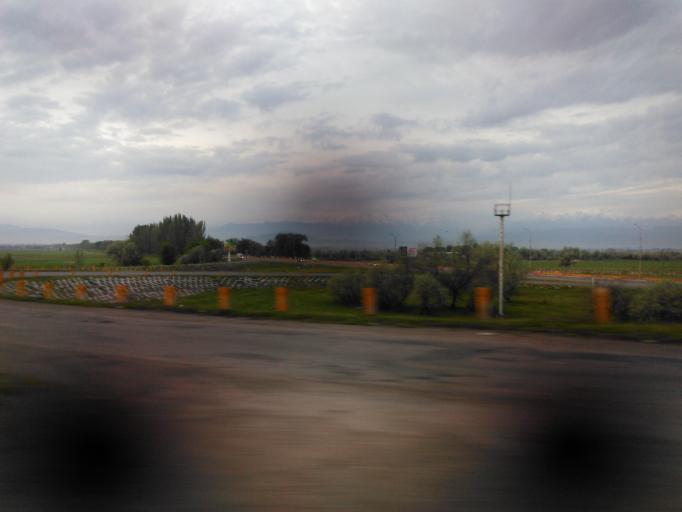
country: KG
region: Chuy
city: Bishkek
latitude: 42.9341
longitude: 74.4950
